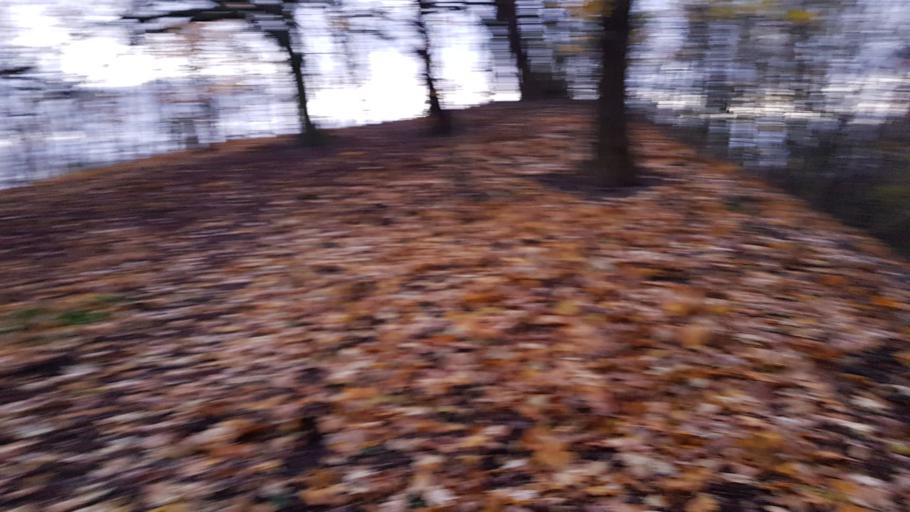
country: PL
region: West Pomeranian Voivodeship
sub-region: Szczecin
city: Szczecin
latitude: 53.4641
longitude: 14.5916
